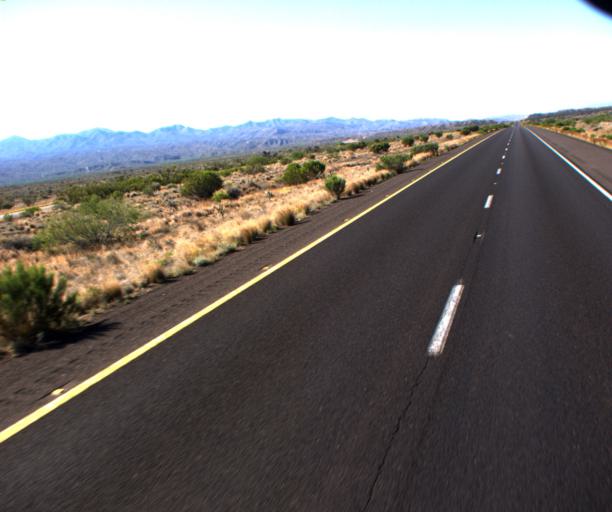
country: US
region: Arizona
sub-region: Mohave County
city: Kingman
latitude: 35.1105
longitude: -113.6667
